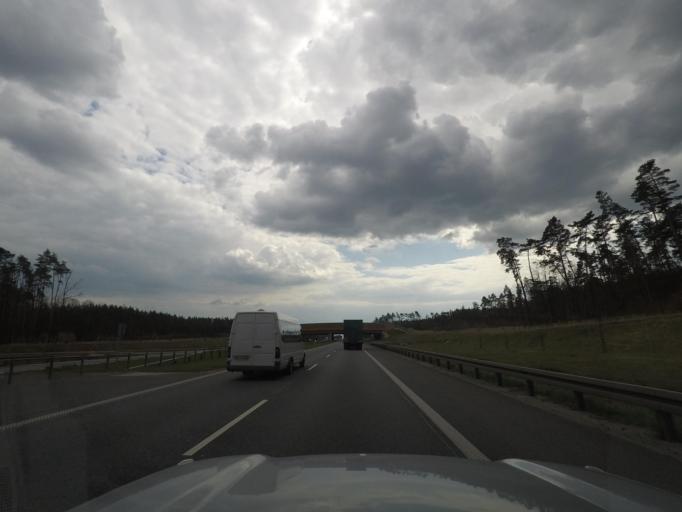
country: PL
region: Lower Silesian Voivodeship
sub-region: Powiat lubinski
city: Osiek
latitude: 51.3256
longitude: 16.1618
